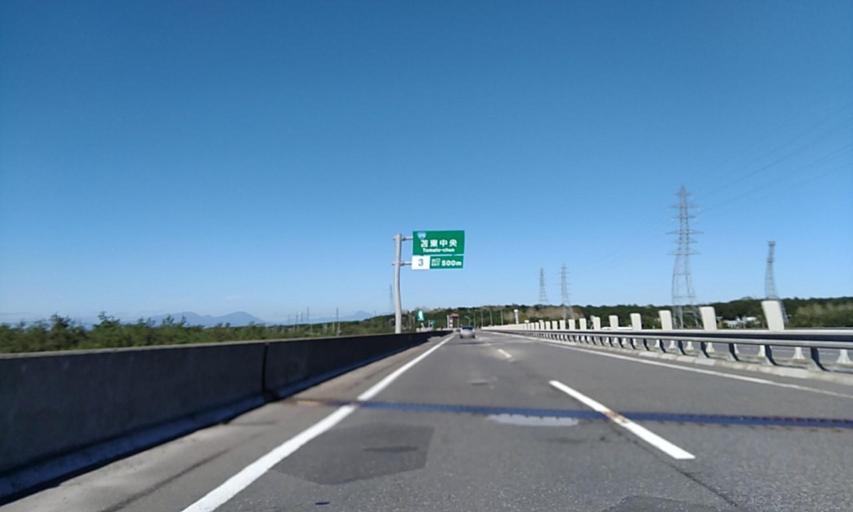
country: JP
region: Hokkaido
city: Tomakomai
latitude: 42.6708
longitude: 141.7903
